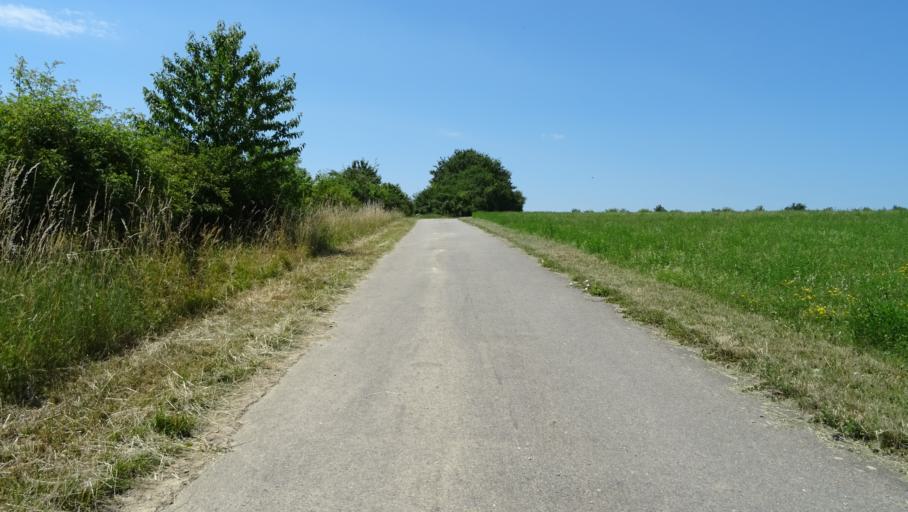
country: DE
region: Baden-Wuerttemberg
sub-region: Karlsruhe Region
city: Mosbach
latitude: 49.3678
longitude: 9.1221
